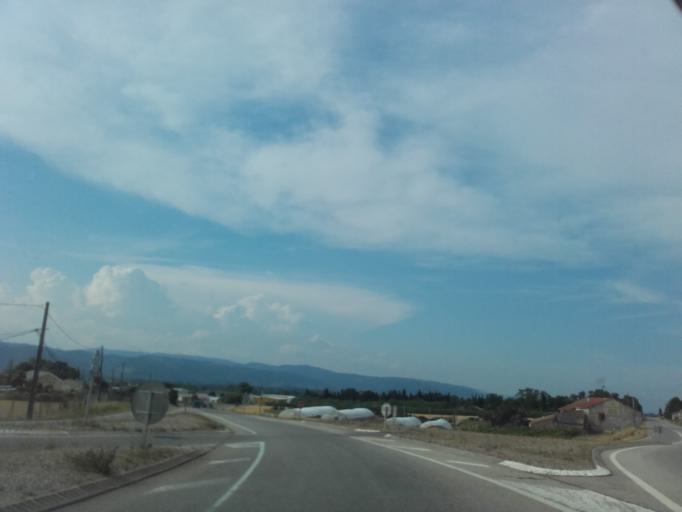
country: FR
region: Rhone-Alpes
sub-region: Departement de la Drome
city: Loriol-sur-Drome
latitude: 44.7333
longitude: 4.8099
